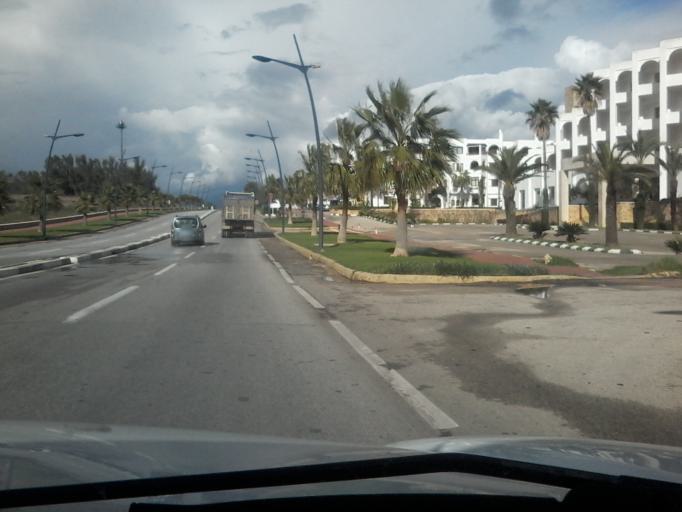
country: ES
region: Ceuta
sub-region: Ceuta
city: Ceuta
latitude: 35.7579
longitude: -5.3479
